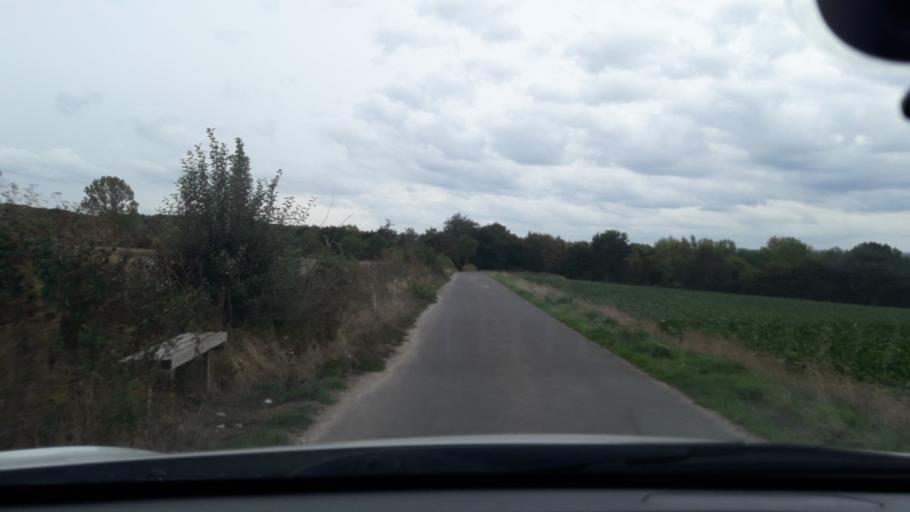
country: DE
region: Lower Saxony
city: Flothe
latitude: 52.0546
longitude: 10.4552
